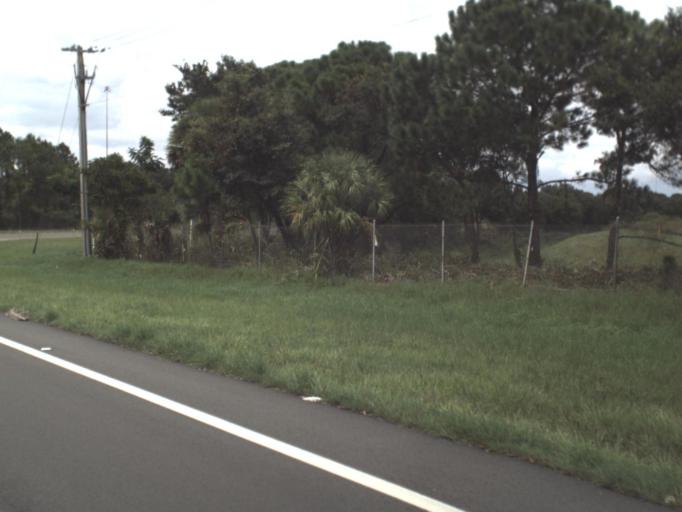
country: US
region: Florida
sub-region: Sarasota County
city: Lake Sarasota
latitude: 27.2989
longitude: -82.4450
